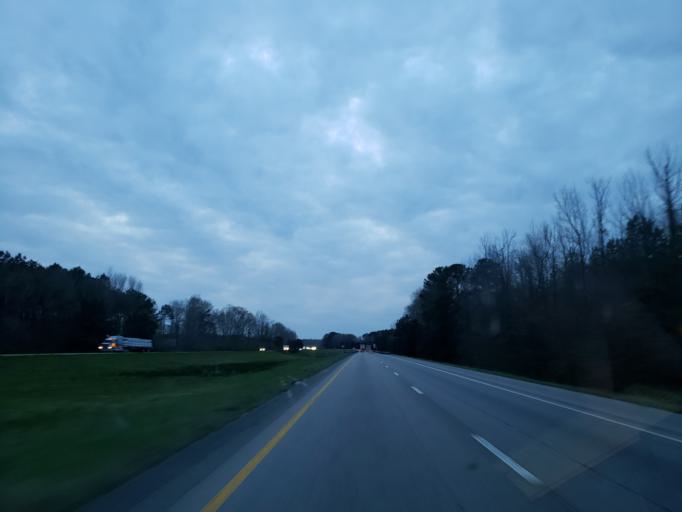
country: US
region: Mississippi
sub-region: Lauderdale County
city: Marion
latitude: 32.4129
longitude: -88.4900
